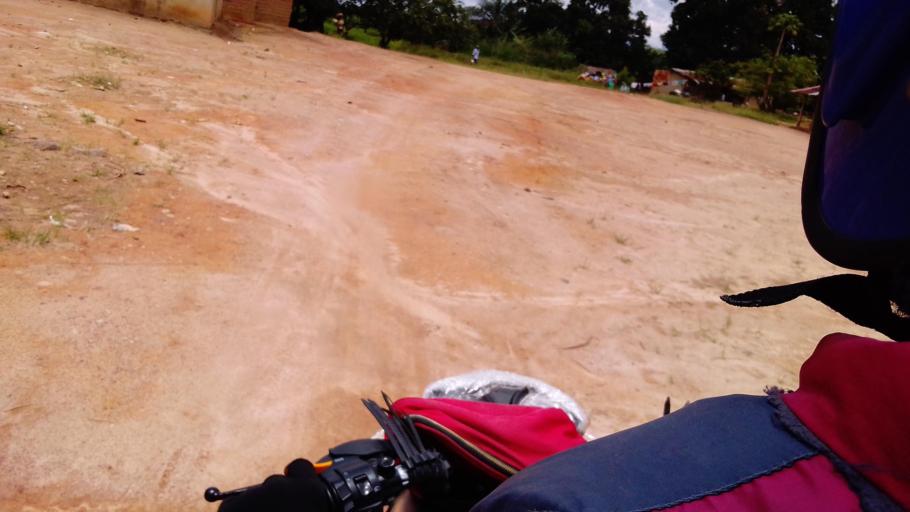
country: SL
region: Eastern Province
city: Koidu
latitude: 8.6775
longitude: -10.9582
